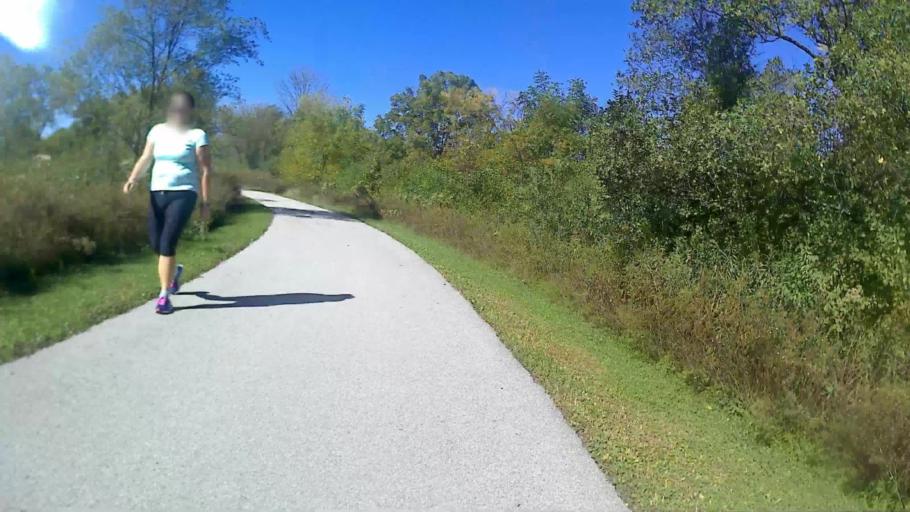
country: US
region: Illinois
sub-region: DuPage County
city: Itasca
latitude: 41.9613
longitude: -88.0059
